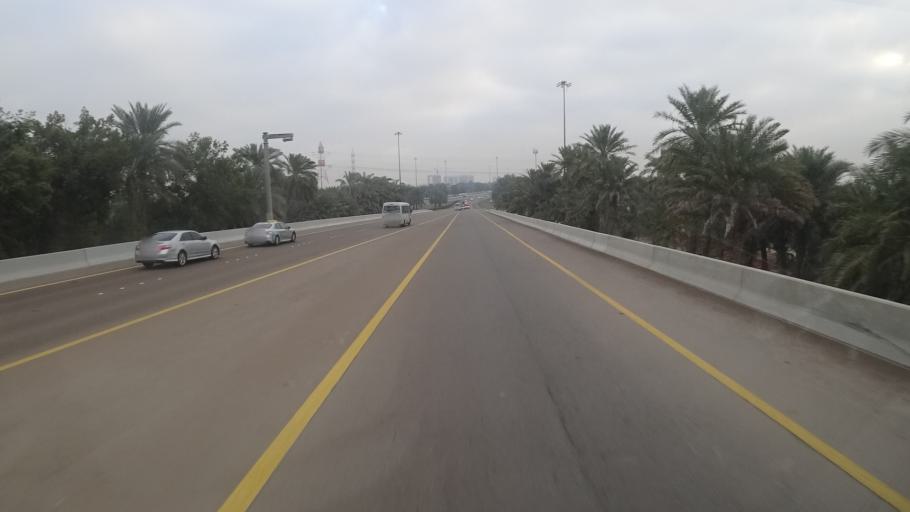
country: AE
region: Abu Dhabi
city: Abu Dhabi
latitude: 24.3907
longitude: 54.5455
